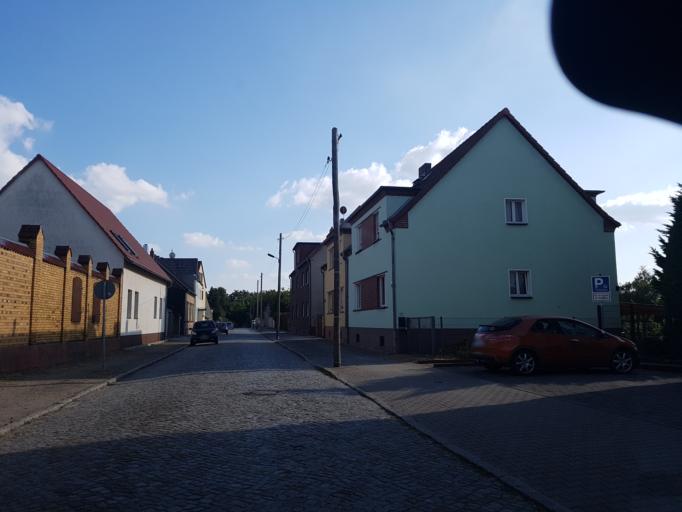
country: DE
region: Saxony-Anhalt
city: Wittenburg
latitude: 51.8668
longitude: 12.6033
